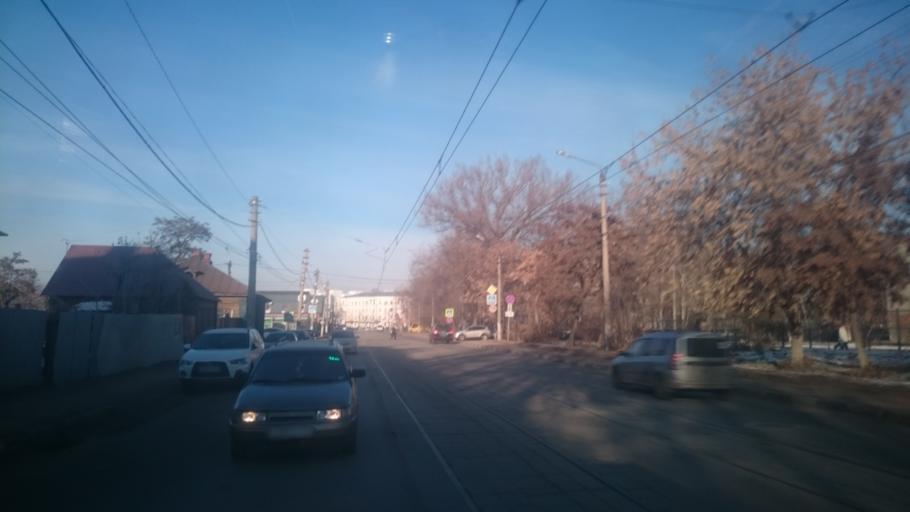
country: RU
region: Tula
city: Tula
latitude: 54.1873
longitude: 37.6238
